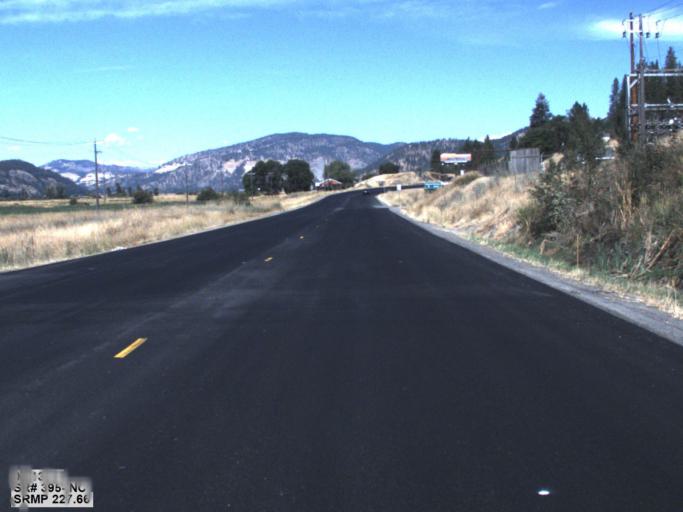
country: US
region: Washington
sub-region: Stevens County
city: Colville
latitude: 48.5178
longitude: -117.9009
